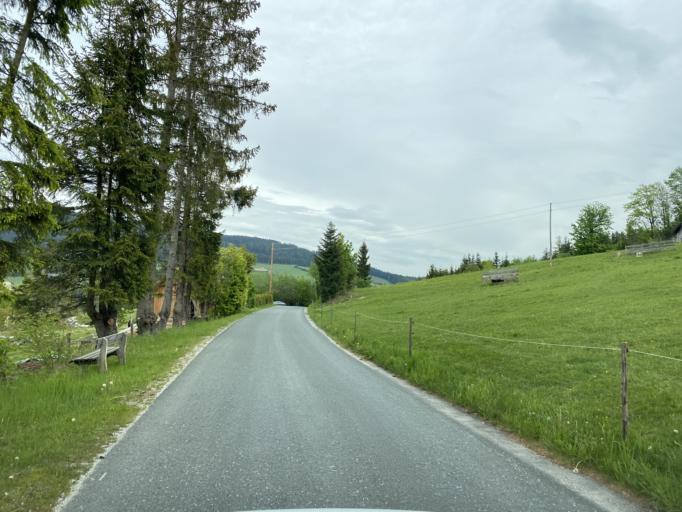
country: AT
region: Styria
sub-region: Politischer Bezirk Weiz
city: Gschaid bei Birkfeld
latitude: 47.3359
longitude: 15.7344
